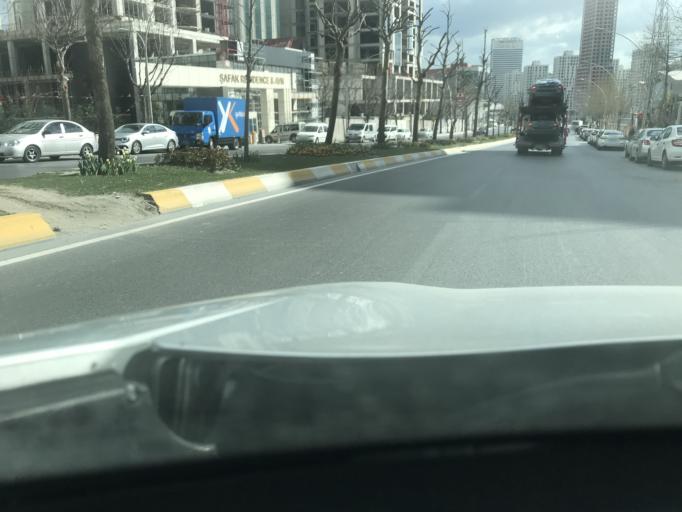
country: TR
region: Istanbul
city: Esenyurt
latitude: 41.0161
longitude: 28.6826
